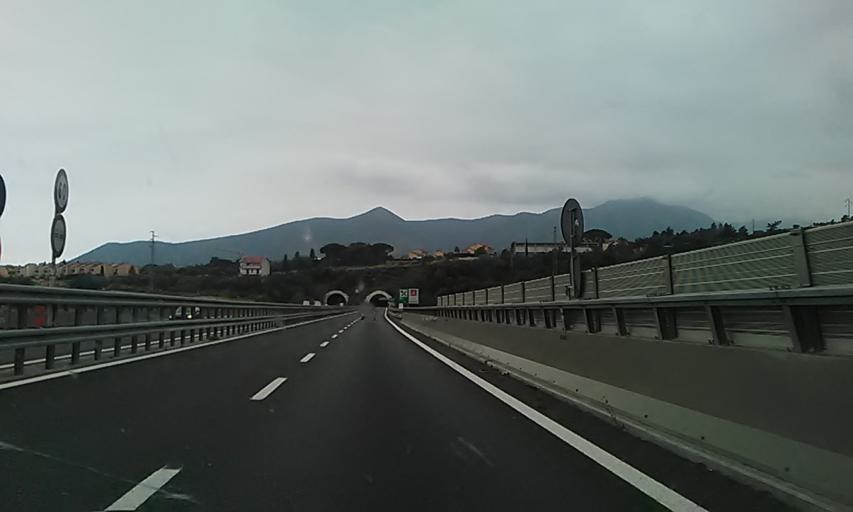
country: IT
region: Liguria
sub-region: Provincia di Savona
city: Loano
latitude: 44.1396
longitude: 8.2441
